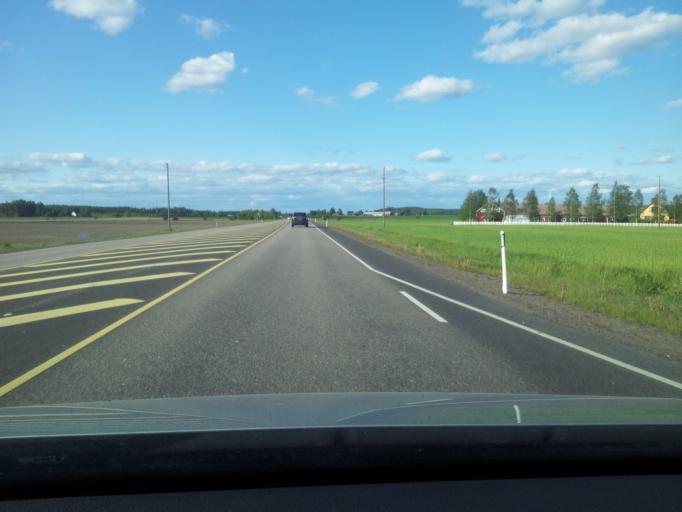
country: FI
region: Kymenlaakso
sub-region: Kouvola
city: Elimaeki
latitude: 60.7444
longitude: 26.4500
